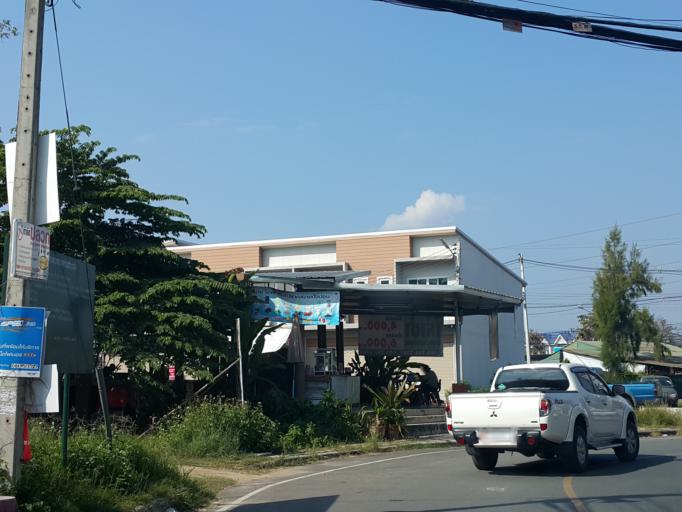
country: TH
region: Chiang Mai
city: San Sai
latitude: 18.8361
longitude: 99.0634
